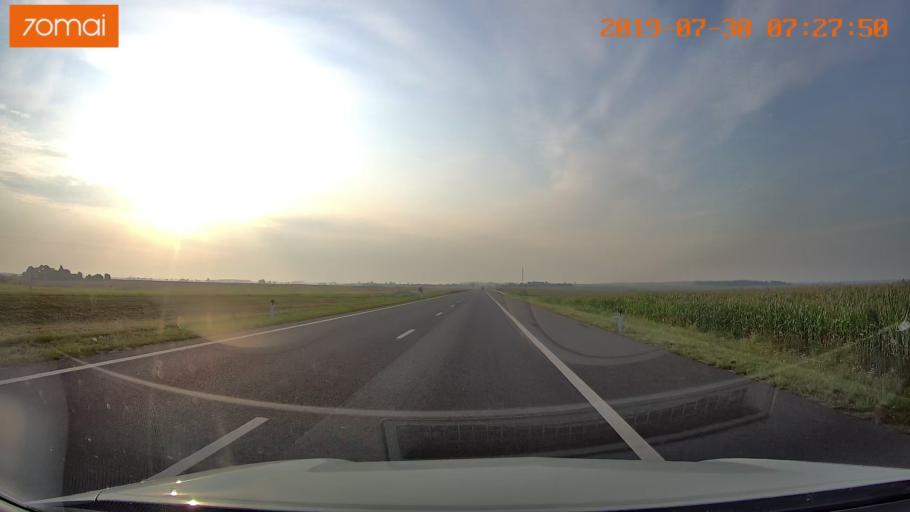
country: RU
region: Kaliningrad
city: Gvardeysk
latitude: 54.6803
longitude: 20.8974
